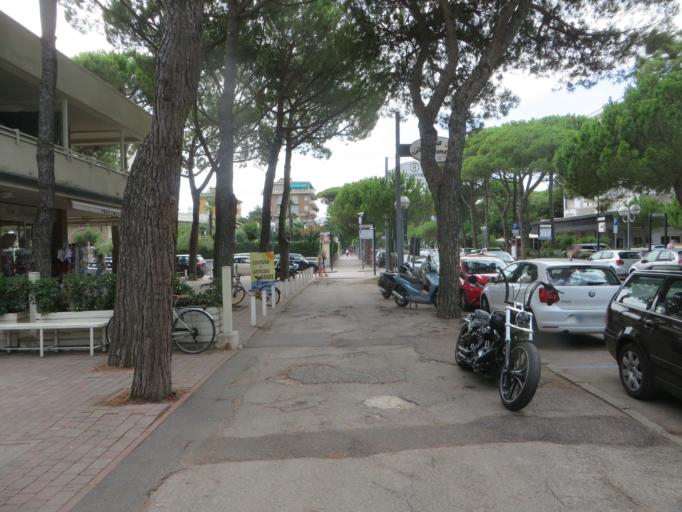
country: IT
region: Emilia-Romagna
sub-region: Provincia di Ravenna
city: Cervia
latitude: 44.2734
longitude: 12.3527
